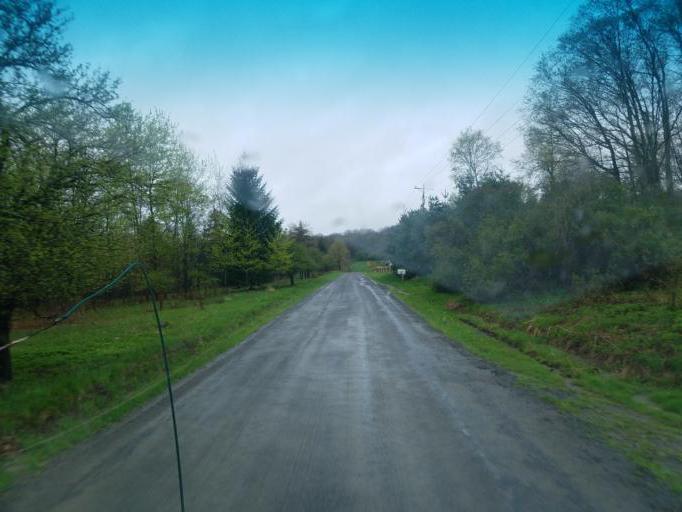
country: US
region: Pennsylvania
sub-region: Tioga County
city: Westfield
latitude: 41.9817
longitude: -77.6934
